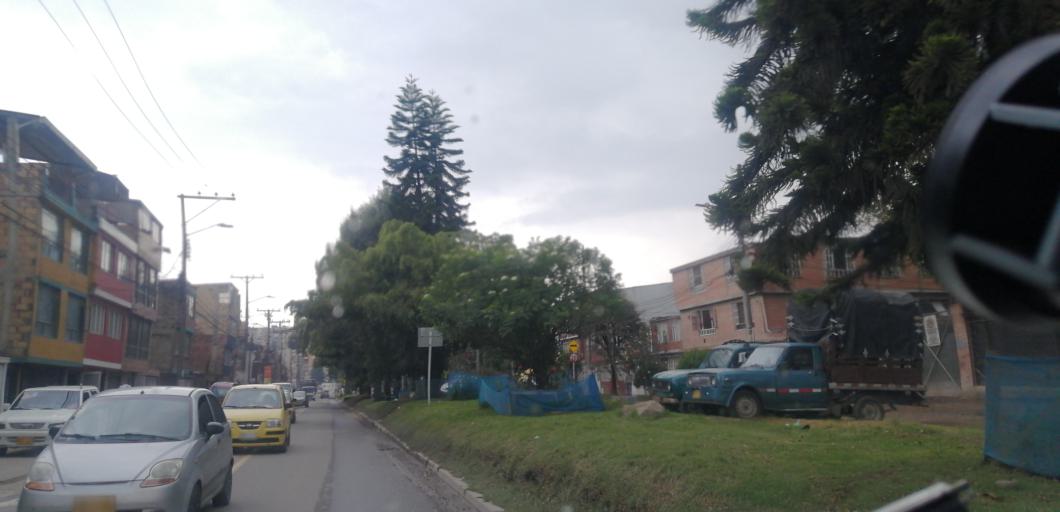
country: CO
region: Cundinamarca
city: Funza
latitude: 4.6854
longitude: -74.1526
